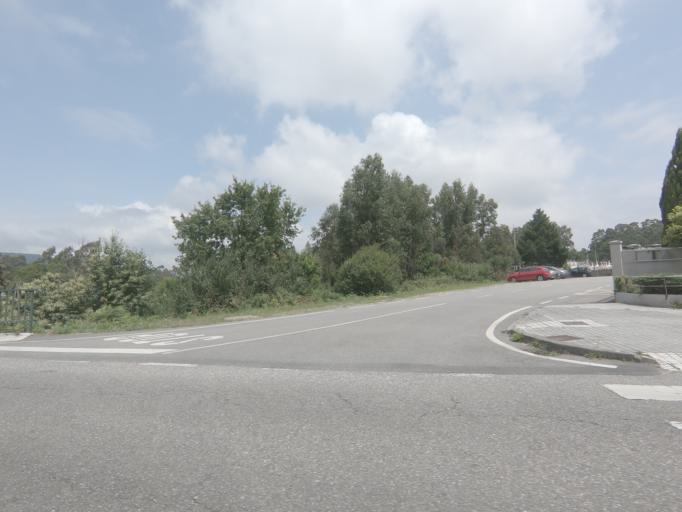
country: ES
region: Galicia
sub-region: Provincia de Pontevedra
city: A Guarda
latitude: 41.8978
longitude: -8.8604
